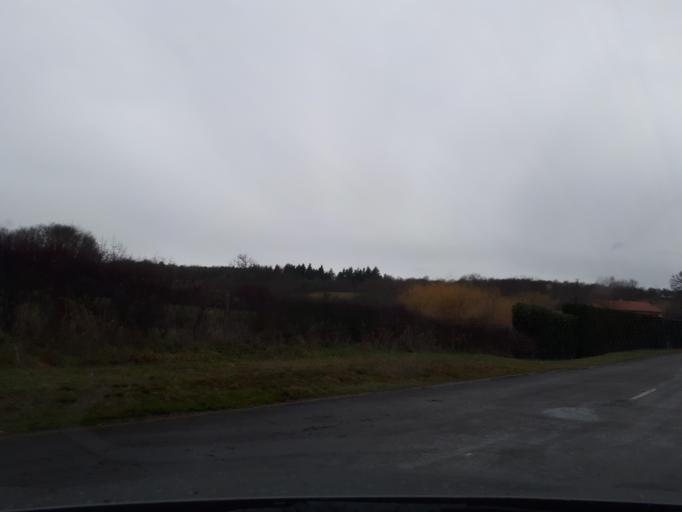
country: FR
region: Rhone-Alpes
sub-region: Departement de la Loire
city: Boen-sur-Lignon
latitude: 45.7690
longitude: 4.0006
